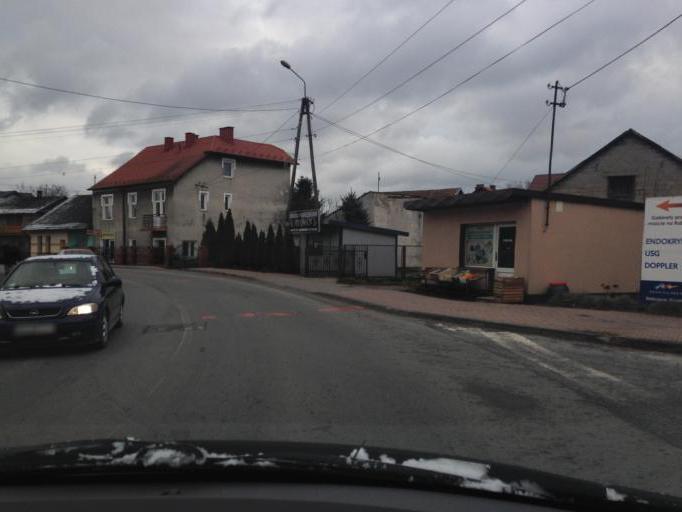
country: PL
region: Lesser Poland Voivodeship
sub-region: Powiat wielicki
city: Gdow
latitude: 49.9070
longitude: 20.1985
